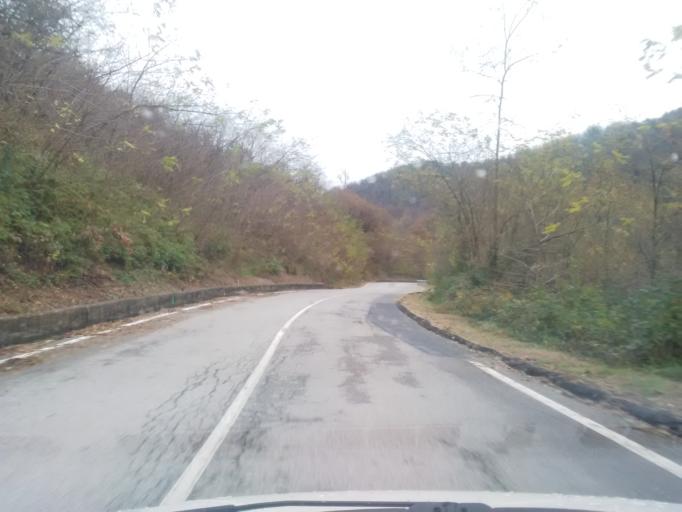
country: IT
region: Piedmont
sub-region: Provincia di Novara
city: Pogno
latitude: 45.7446
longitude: 8.3729
